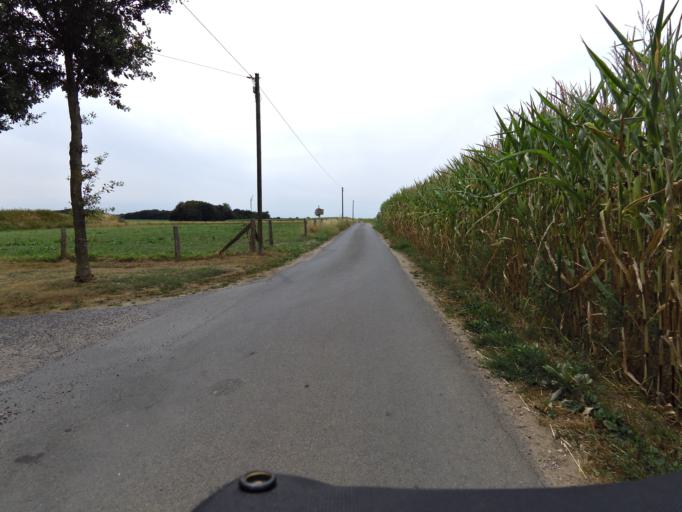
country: DE
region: North Rhine-Westphalia
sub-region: Regierungsbezirk Dusseldorf
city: Weeze
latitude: 51.5858
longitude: 6.1842
